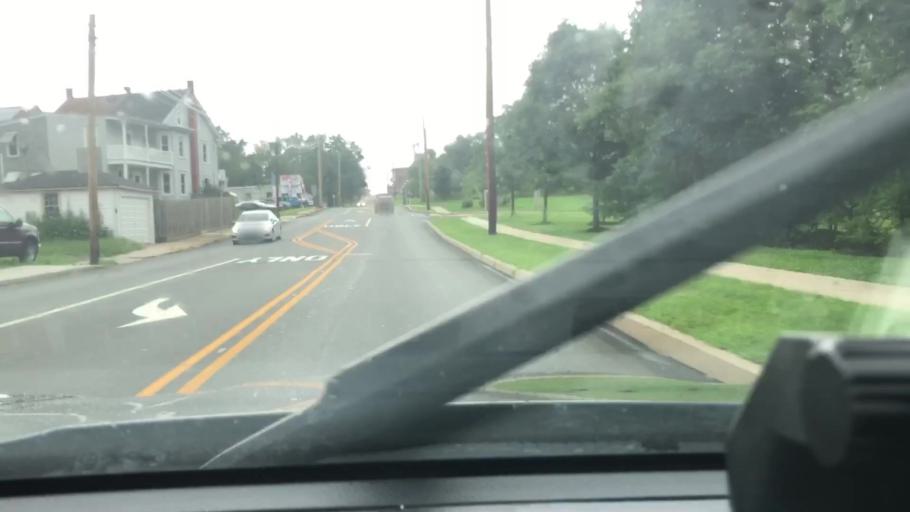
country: US
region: Pennsylvania
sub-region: Montgomery County
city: Pennsburg
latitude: 40.3952
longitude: -75.5001
